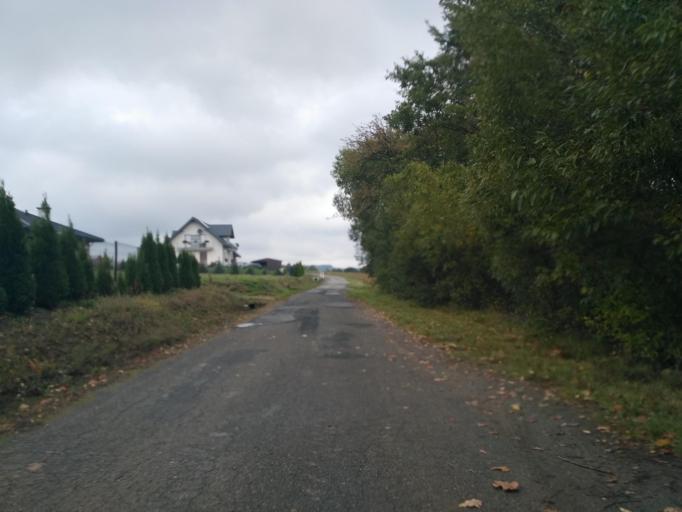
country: PL
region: Subcarpathian Voivodeship
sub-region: Powiat debicki
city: Brzostek
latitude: 49.9248
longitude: 21.4465
